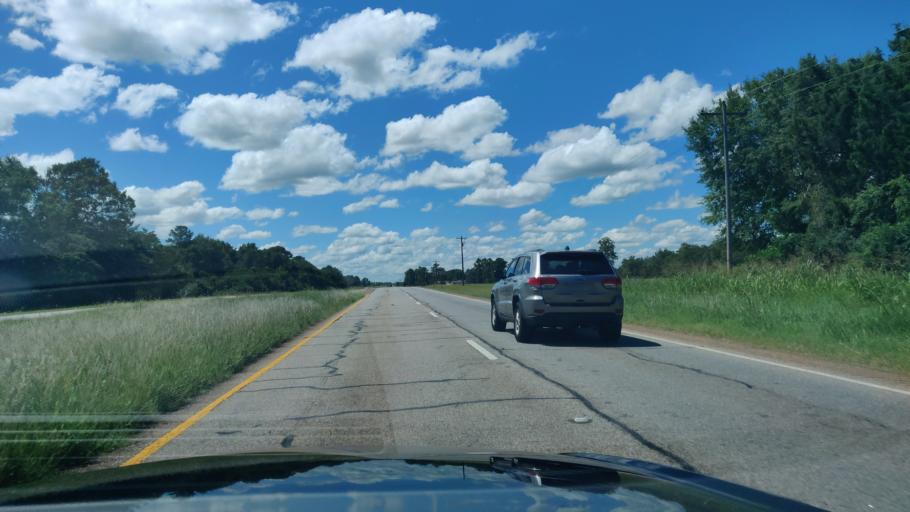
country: US
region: Georgia
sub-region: Webster County
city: Preston
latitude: 31.9270
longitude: -84.5549
